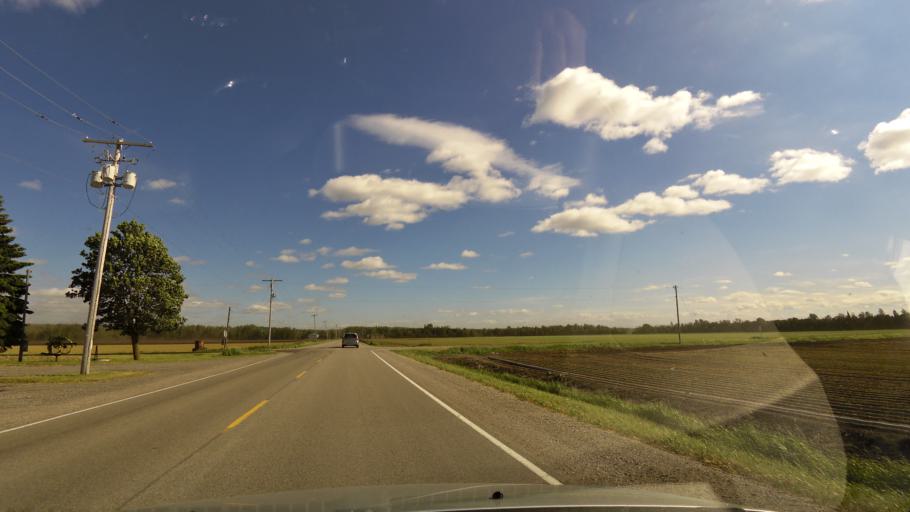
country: CA
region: Ontario
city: Innisfil
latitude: 44.2195
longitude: -79.6315
